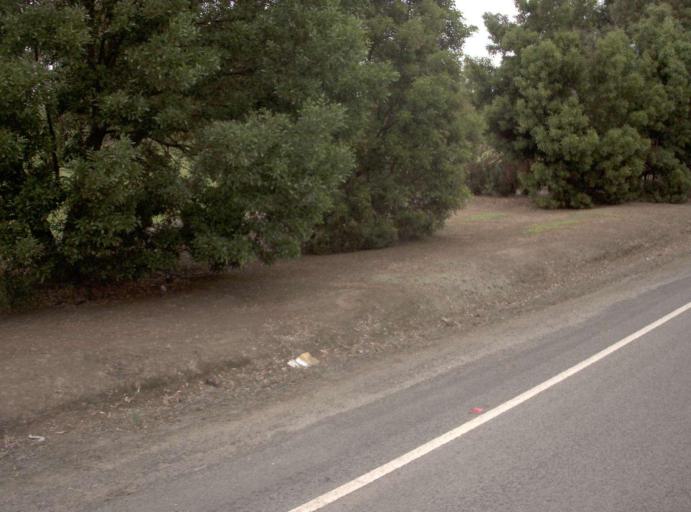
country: AU
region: Victoria
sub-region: Bass Coast
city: North Wonthaggi
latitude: -38.5349
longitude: 145.9504
